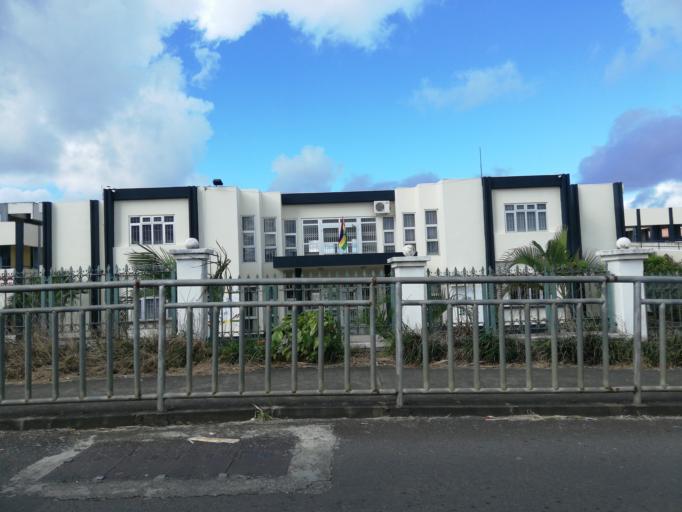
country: MU
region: Flacq
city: Camp de Masque
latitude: -20.2310
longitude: 57.6788
